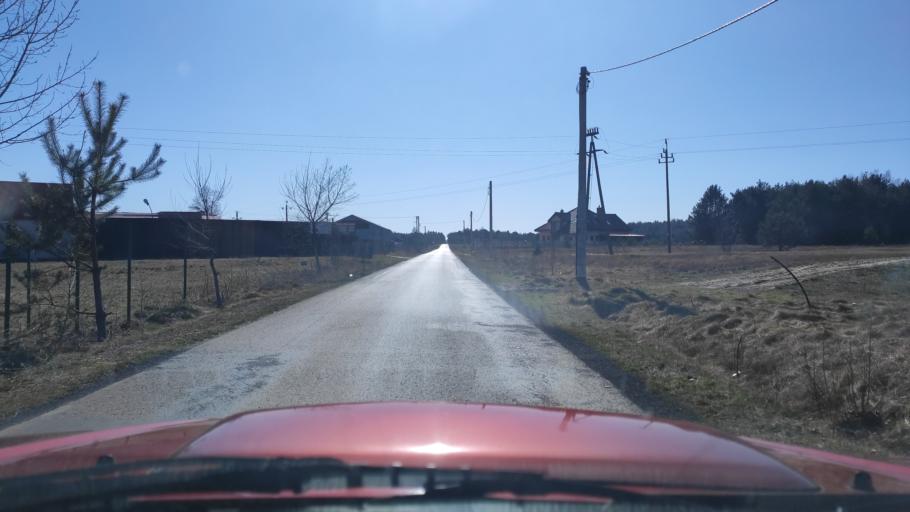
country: PL
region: Masovian Voivodeship
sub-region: Powiat radomski
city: Pionki
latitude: 51.5209
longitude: 21.4720
